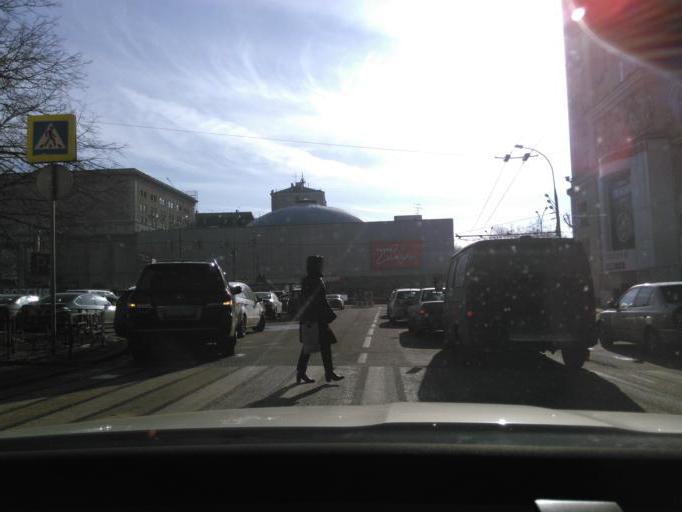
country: RU
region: Moscow
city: Moscow
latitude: 55.7692
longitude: 37.5936
